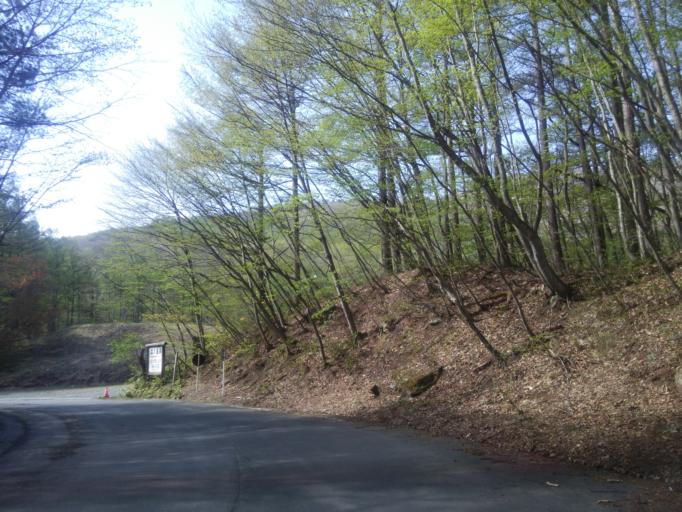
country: JP
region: Fukushima
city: Nihommatsu
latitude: 37.6411
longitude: 140.3320
